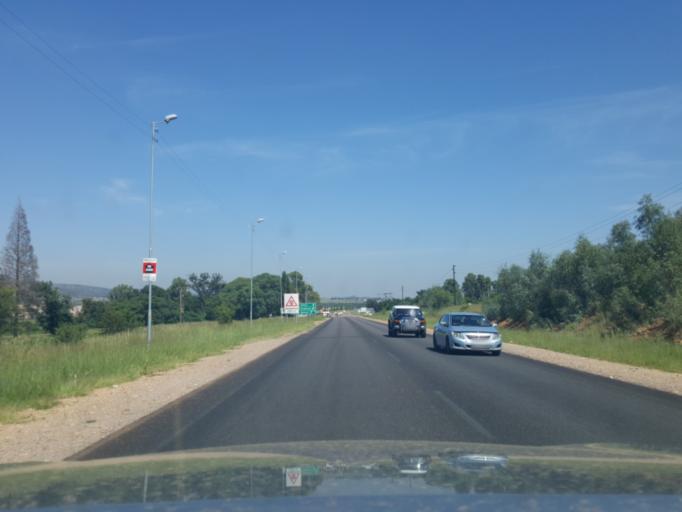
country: ZA
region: Gauteng
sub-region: City of Tshwane Metropolitan Municipality
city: Cullinan
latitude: -25.6831
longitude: 28.4219
